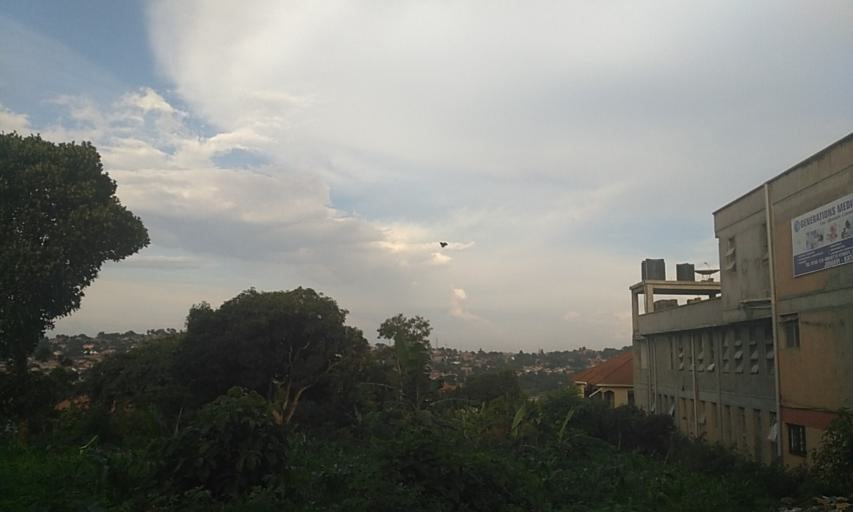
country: UG
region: Central Region
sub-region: Wakiso District
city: Kajansi
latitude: 0.2561
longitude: 32.5334
